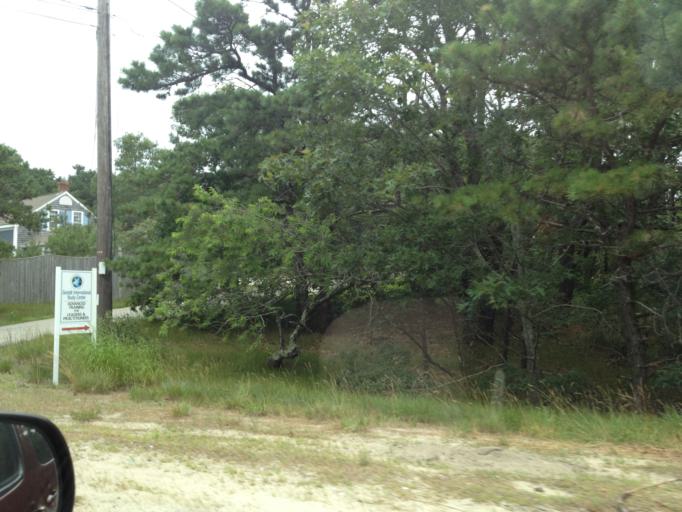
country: US
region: Massachusetts
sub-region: Barnstable County
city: North Eastham
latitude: 41.9090
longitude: -69.9862
